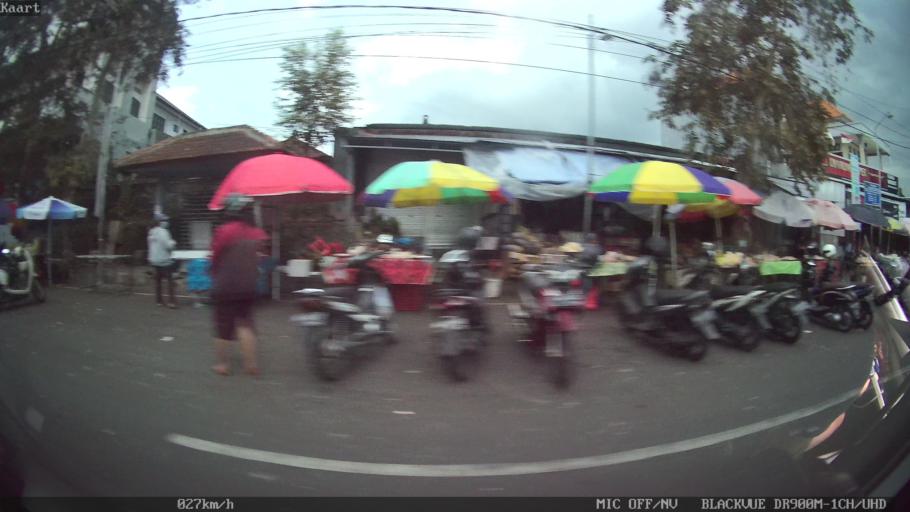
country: ID
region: Bali
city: Banjar Tegal Belodan
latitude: -8.5376
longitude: 115.1178
